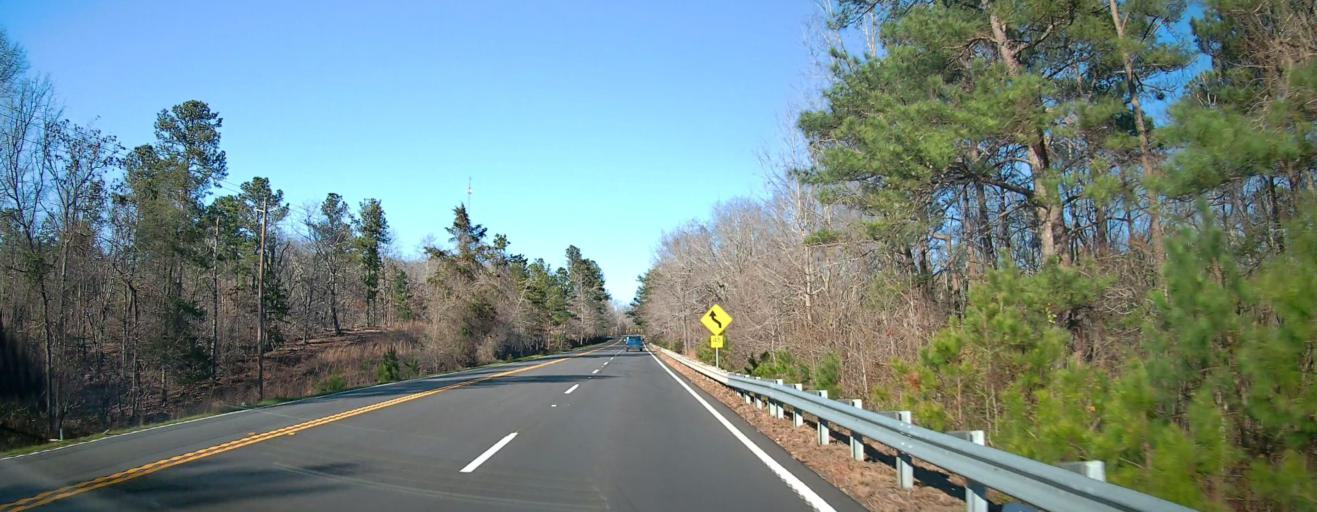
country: US
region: Georgia
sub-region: Talbot County
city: Sardis
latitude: 32.8406
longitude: -84.6956
